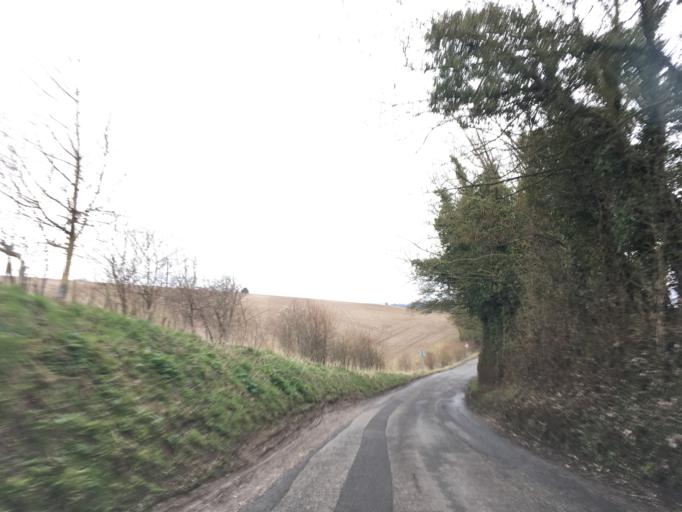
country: GB
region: England
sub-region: West Berkshire
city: Hungerford
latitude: 51.4259
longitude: -1.5131
